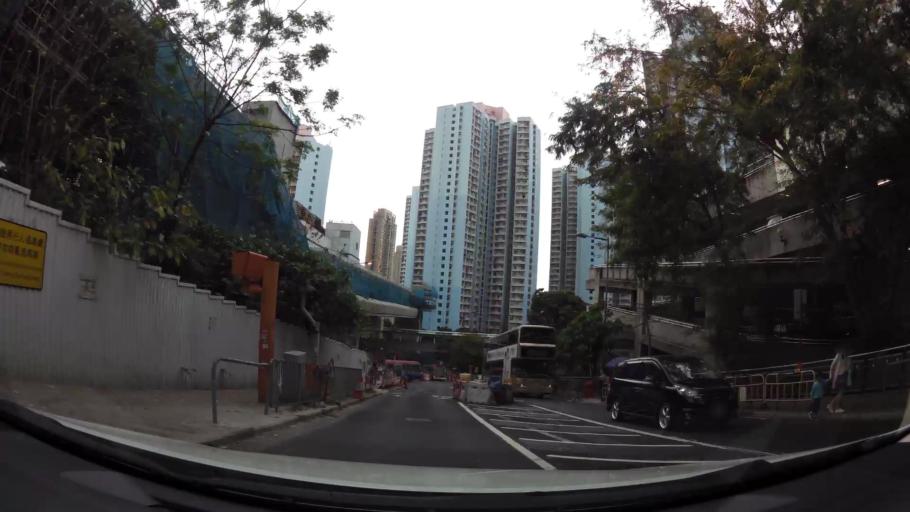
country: HK
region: Wong Tai Sin
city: Wong Tai Sin
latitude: 22.3497
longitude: 114.2000
